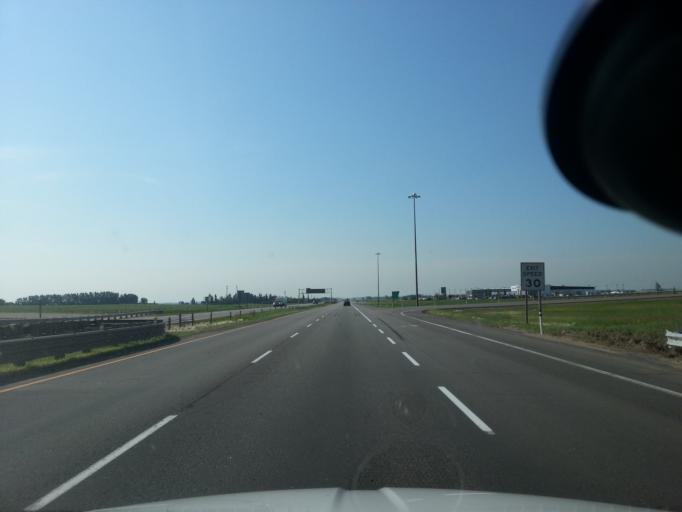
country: CA
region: Alberta
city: Olds
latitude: 51.7946
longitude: -114.0256
